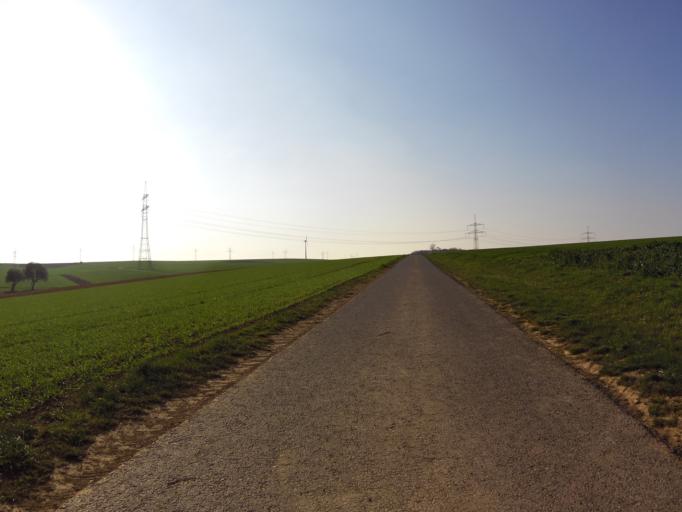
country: DE
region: Bavaria
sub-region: Regierungsbezirk Unterfranken
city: Biebelried
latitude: 49.7682
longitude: 10.0575
